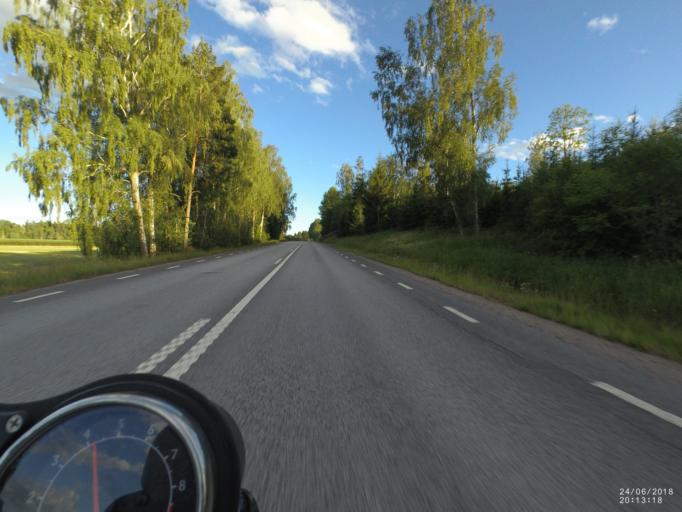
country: SE
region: Soedermanland
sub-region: Nykopings Kommun
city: Nykoping
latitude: 58.8041
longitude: 17.0820
